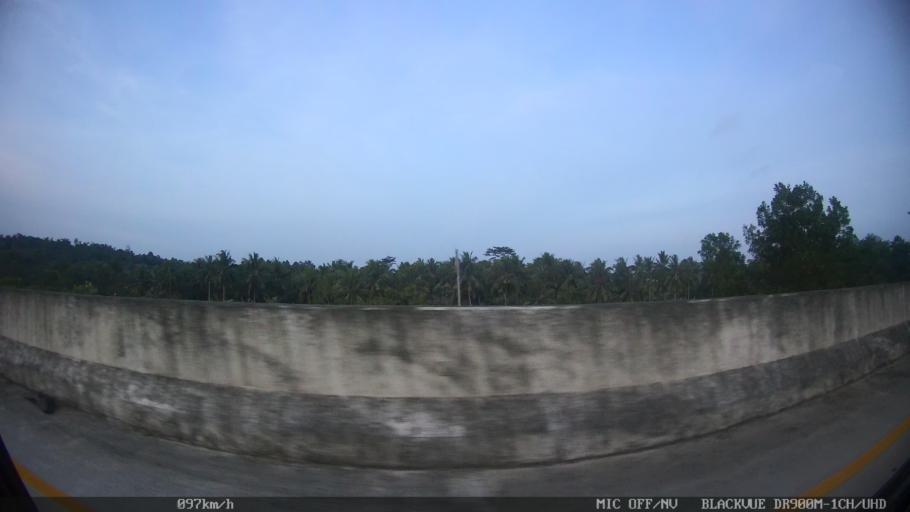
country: ID
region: Lampung
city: Penengahan
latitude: -5.7806
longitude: 105.7210
